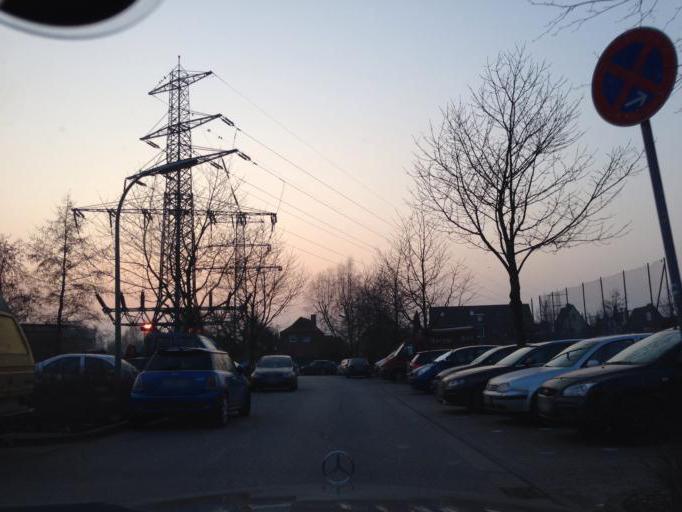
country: DE
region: Hamburg
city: Farmsen-Berne
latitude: 53.5942
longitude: 10.1003
